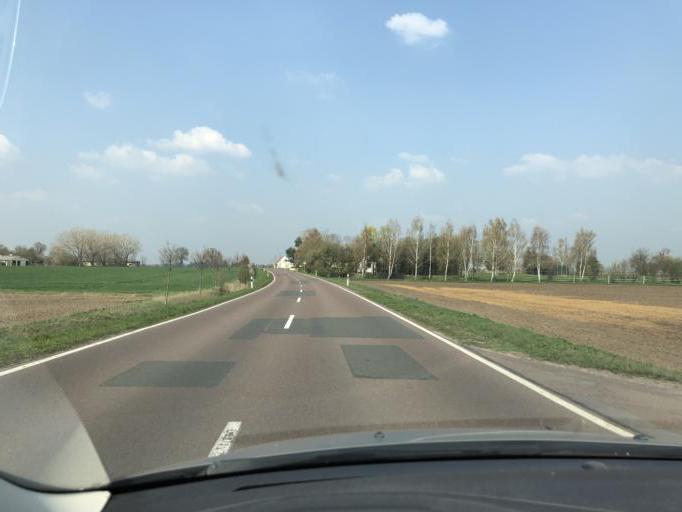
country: DE
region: Saxony-Anhalt
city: Zorbig
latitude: 51.5982
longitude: 12.1328
